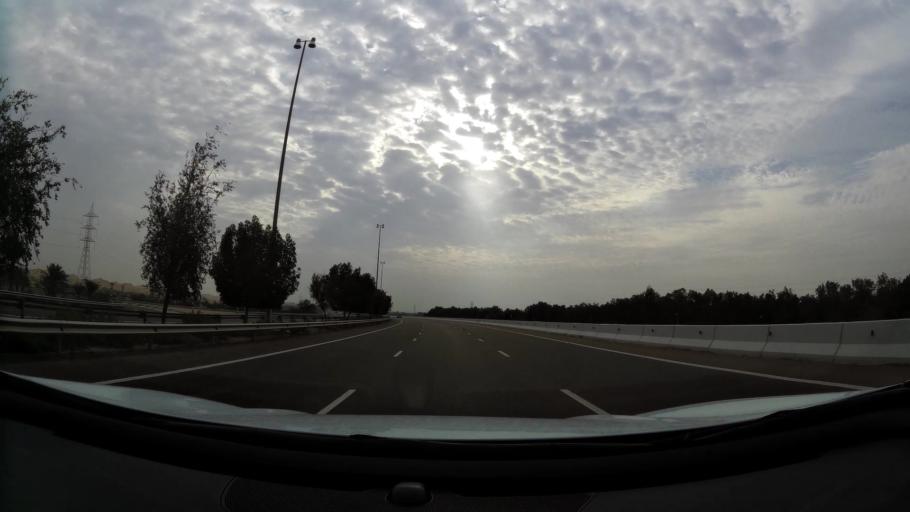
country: AE
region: Abu Dhabi
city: Al Ain
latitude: 24.1813
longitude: 55.0355
